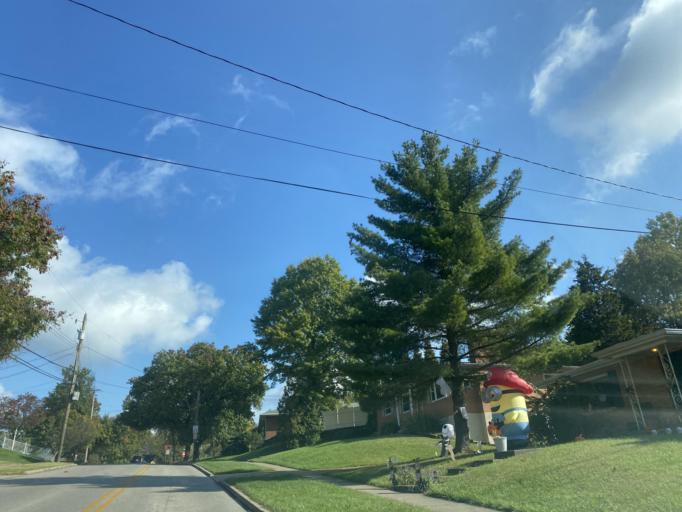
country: US
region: Kentucky
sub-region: Campbell County
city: Fort Thomas
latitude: 39.0949
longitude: -84.4561
